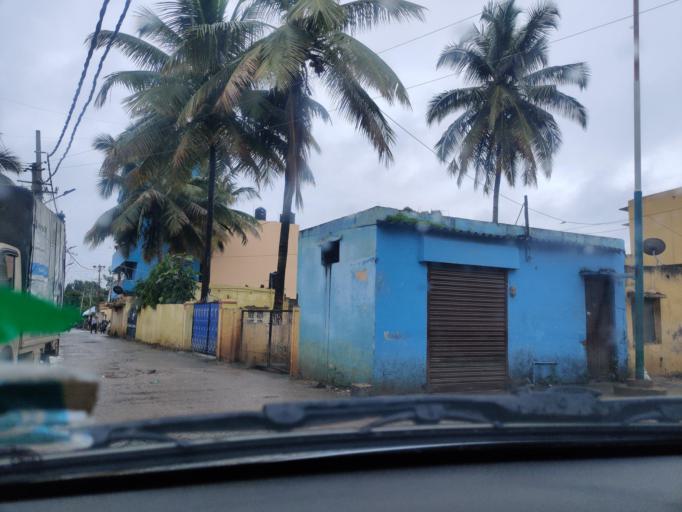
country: IN
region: Karnataka
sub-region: Bangalore Urban
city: Bangalore
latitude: 13.0280
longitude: 77.6423
